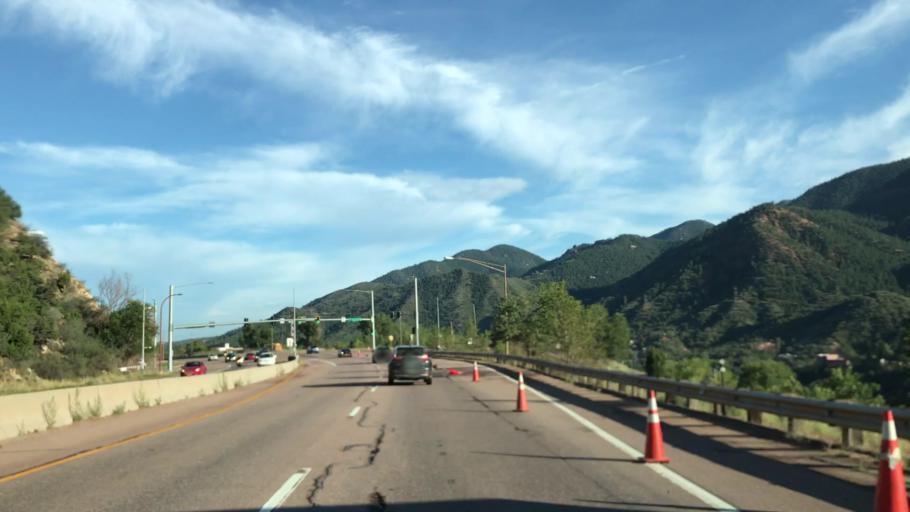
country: US
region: Colorado
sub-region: El Paso County
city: Manitou Springs
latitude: 38.8665
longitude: -104.9220
